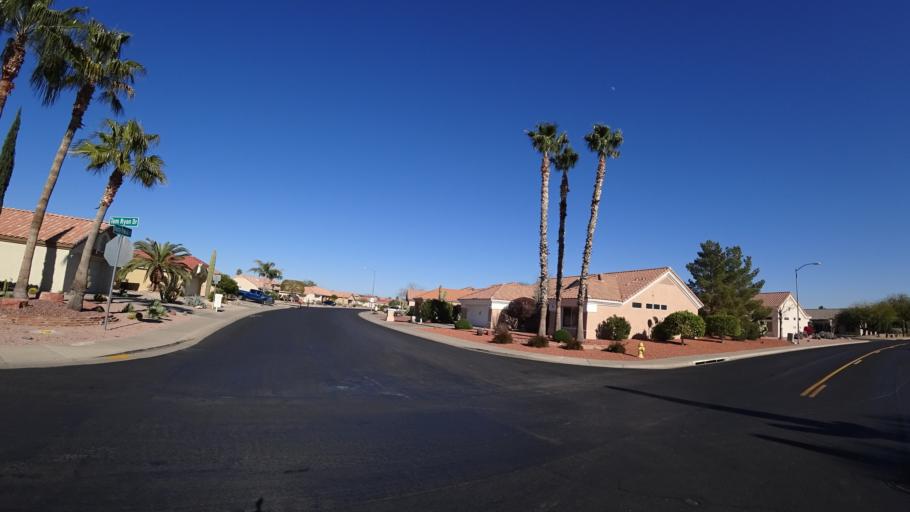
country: US
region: Arizona
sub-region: Maricopa County
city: Sun City West
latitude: 33.6933
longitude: -112.3706
